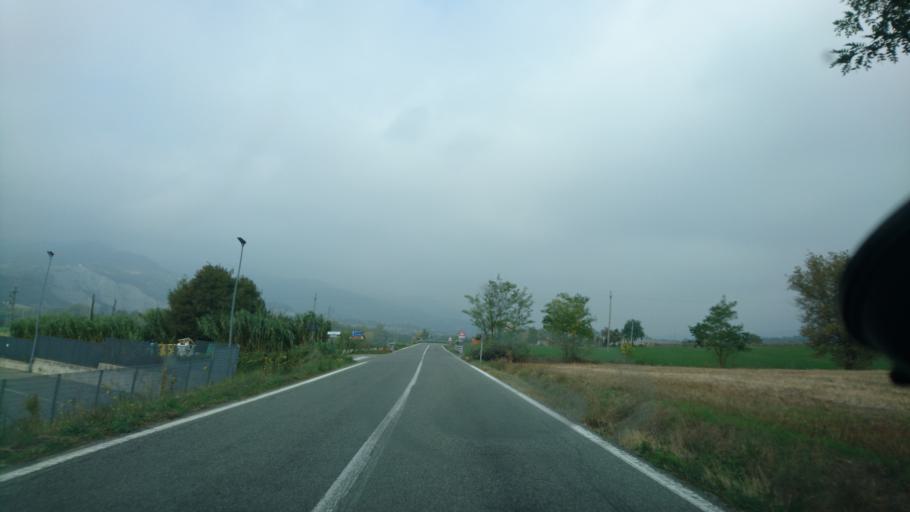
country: IT
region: Piedmont
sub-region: Provincia di Asti
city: Mombaldone
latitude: 44.5647
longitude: 8.3461
